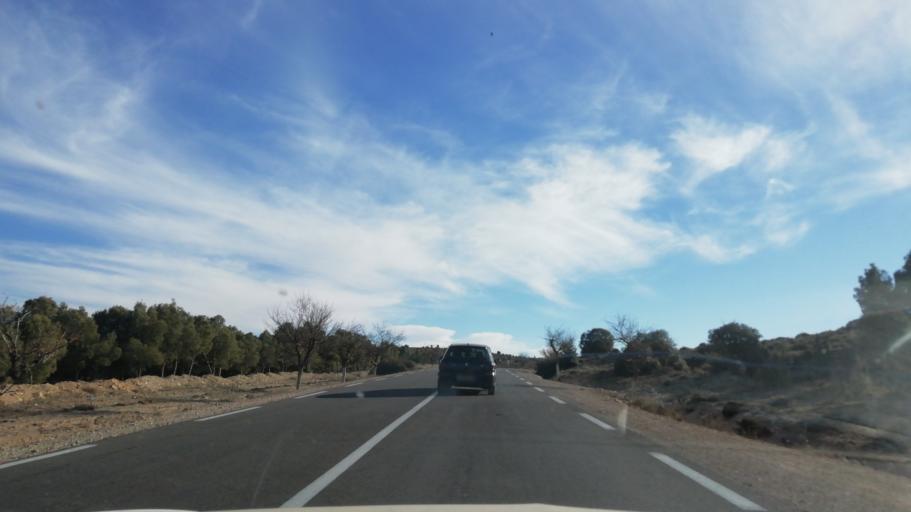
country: DZ
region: Tlemcen
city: Sebdou
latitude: 34.5883
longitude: -1.3178
